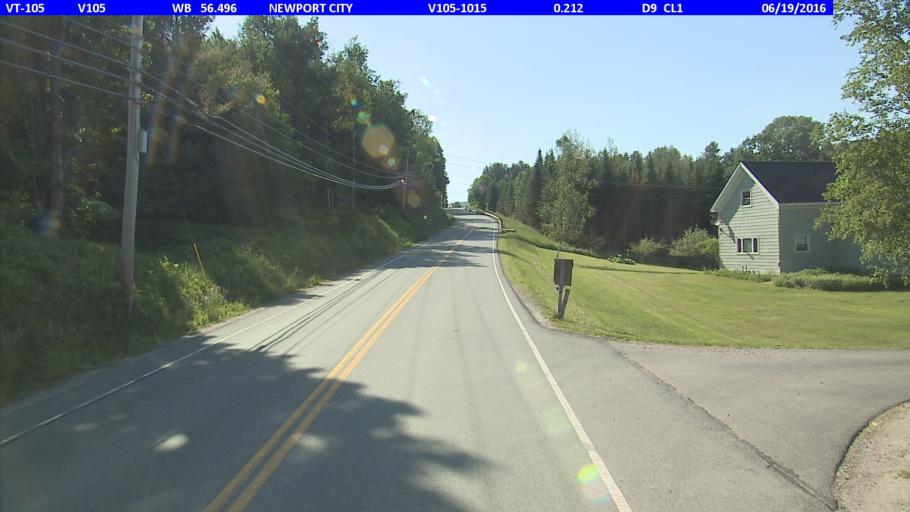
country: US
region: Vermont
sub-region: Orleans County
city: Newport
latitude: 44.9310
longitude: -72.2376
